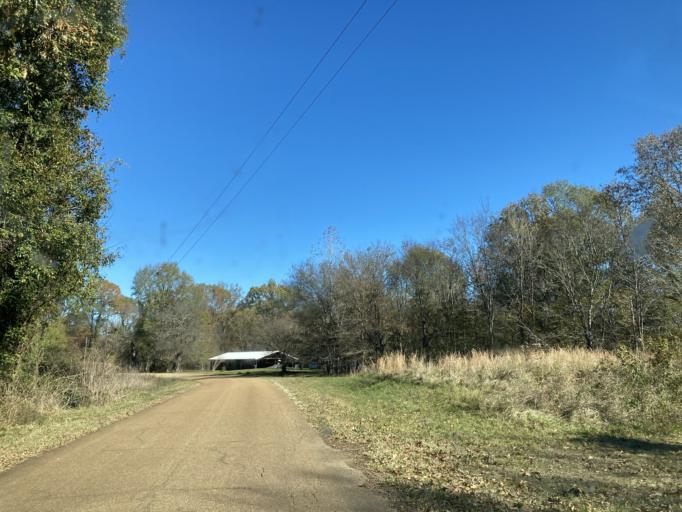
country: US
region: Mississippi
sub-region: Hinds County
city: Lynchburg
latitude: 32.5872
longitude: -90.5209
